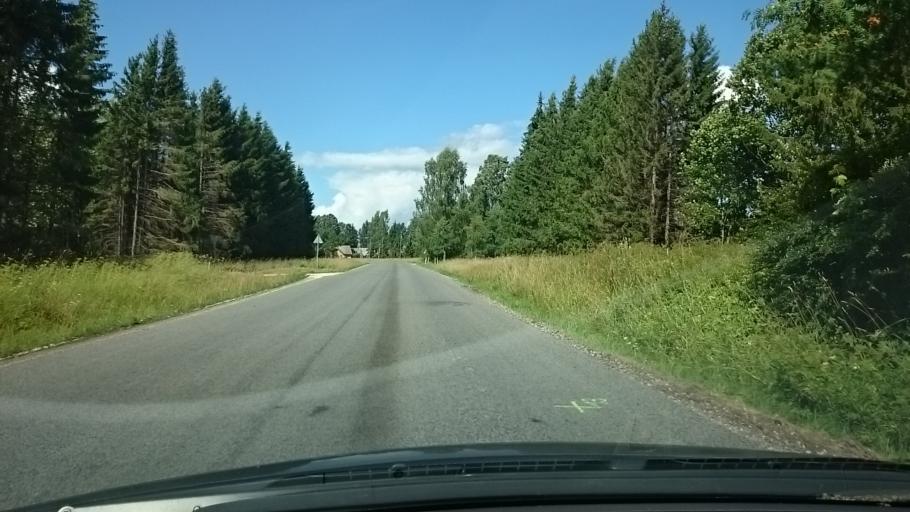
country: EE
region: Polvamaa
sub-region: Polva linn
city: Polva
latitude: 57.9693
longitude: 26.9600
